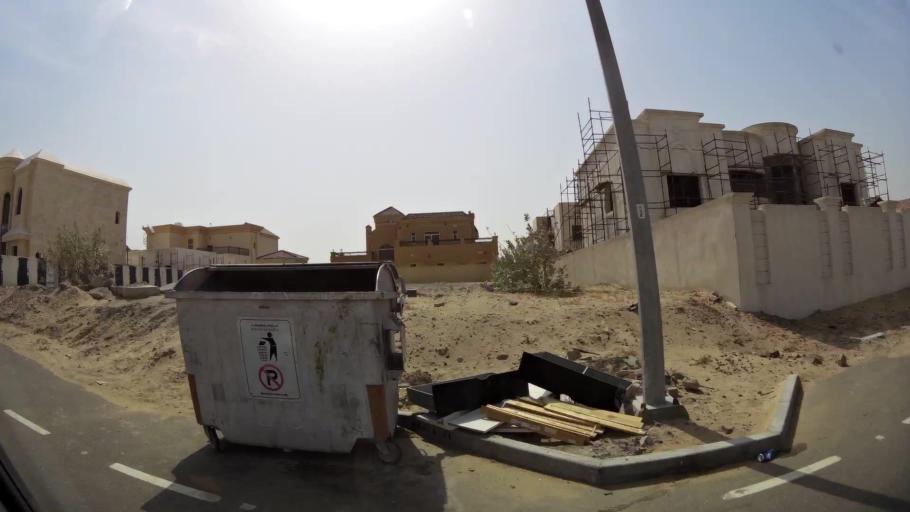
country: AE
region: Ash Shariqah
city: Sharjah
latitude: 25.2675
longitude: 55.4687
